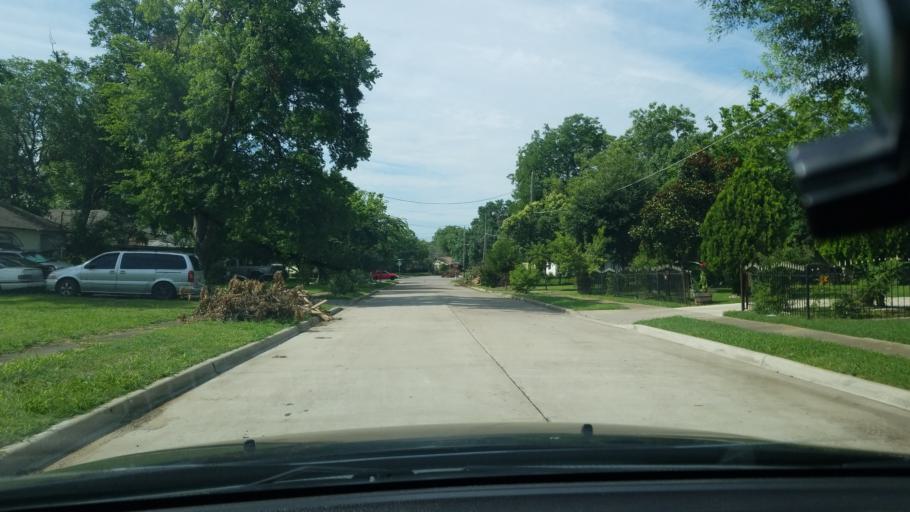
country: US
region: Texas
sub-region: Dallas County
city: Balch Springs
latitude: 32.7646
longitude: -96.6700
